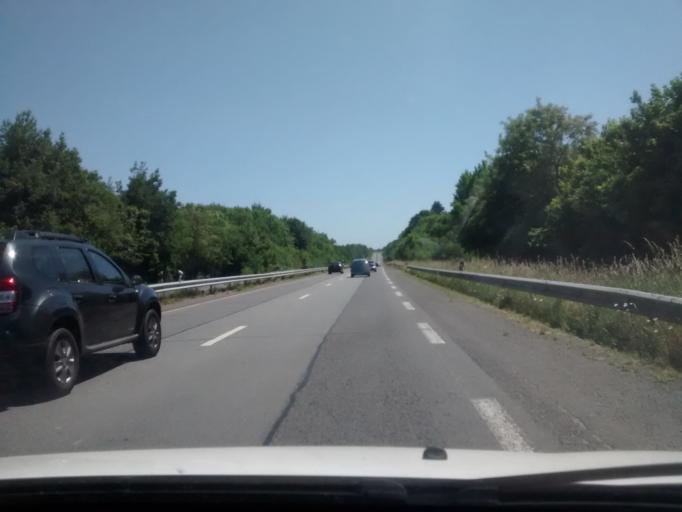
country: FR
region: Brittany
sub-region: Departement d'Ille-et-Vilaine
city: Miniac-Morvan
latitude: 48.5144
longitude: -1.9124
